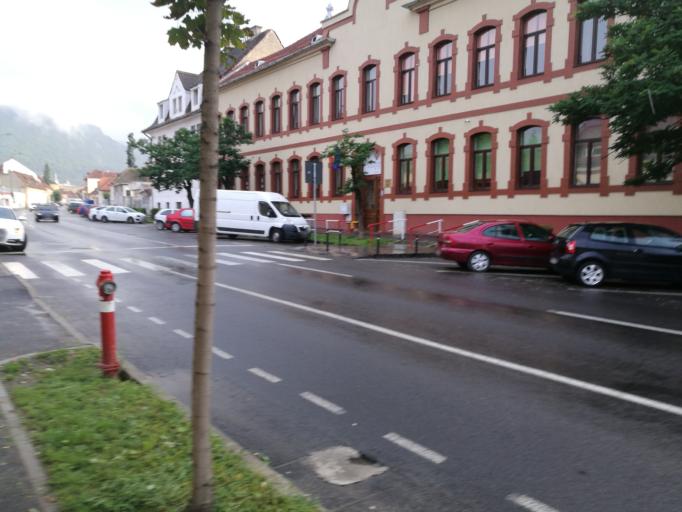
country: RO
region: Brasov
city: Brasov
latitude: 45.6543
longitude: 25.5868
